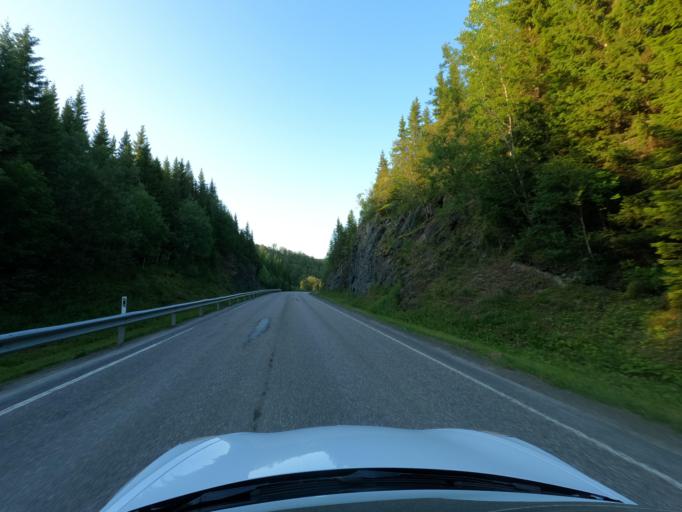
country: NO
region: Troms
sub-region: Harstad
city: Harstad
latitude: 68.7180
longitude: 16.5093
